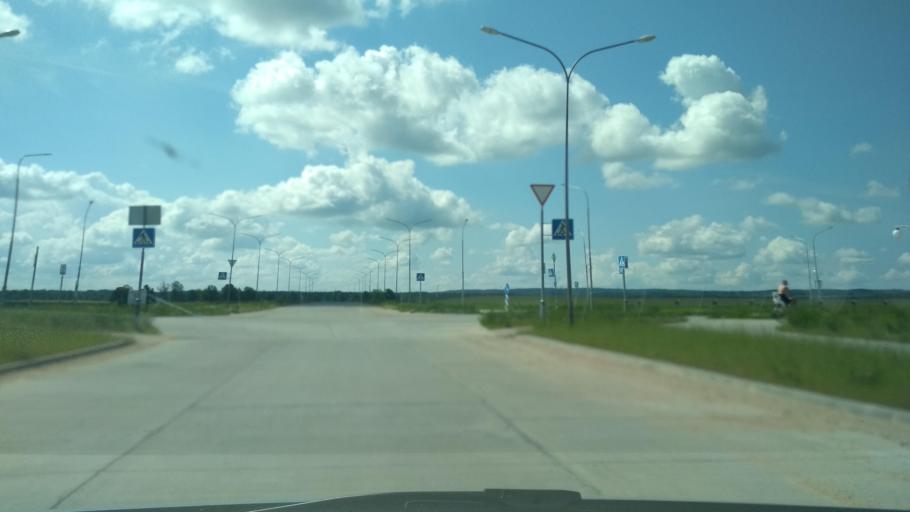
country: BY
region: Grodnenskaya
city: Astravyets
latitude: 54.5989
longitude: 25.9614
